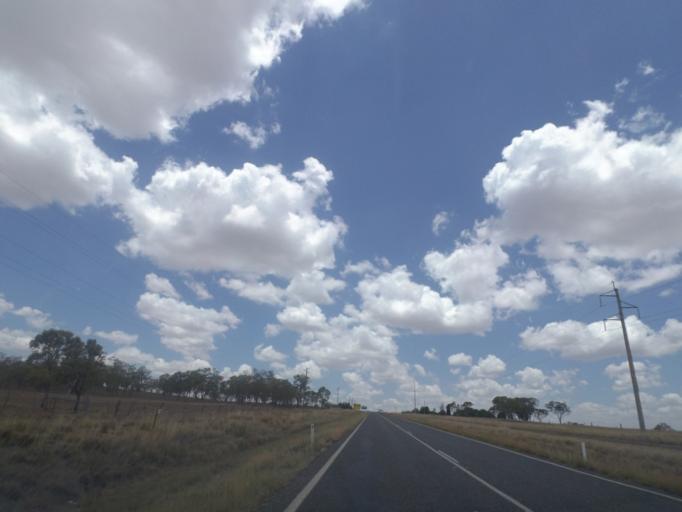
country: AU
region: Queensland
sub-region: Toowoomba
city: Top Camp
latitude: -27.8815
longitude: 151.9700
